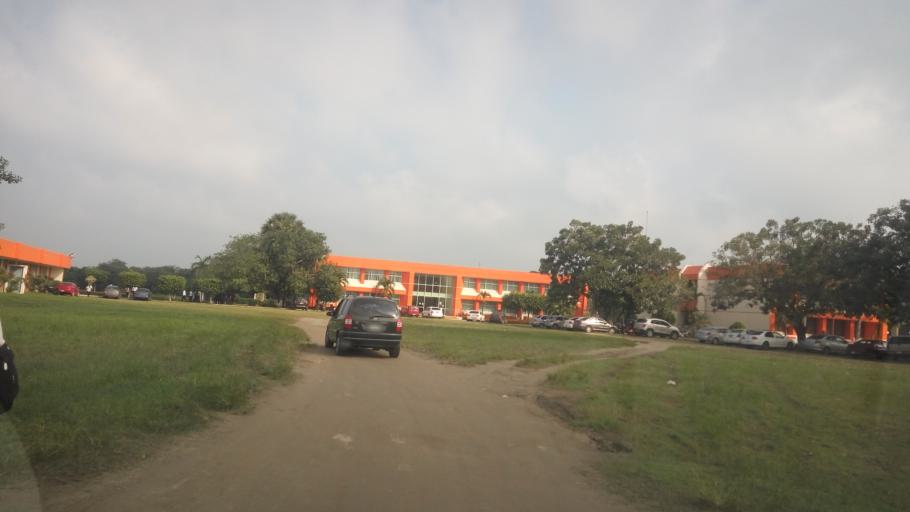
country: MX
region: Tabasco
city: Frontera
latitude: 18.5315
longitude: -92.6341
